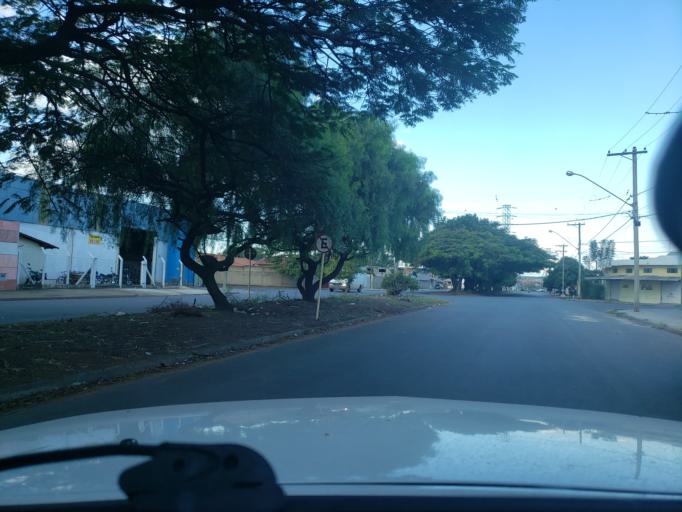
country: BR
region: Sao Paulo
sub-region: Moji-Guacu
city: Mogi-Gaucu
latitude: -22.3229
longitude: -46.9240
